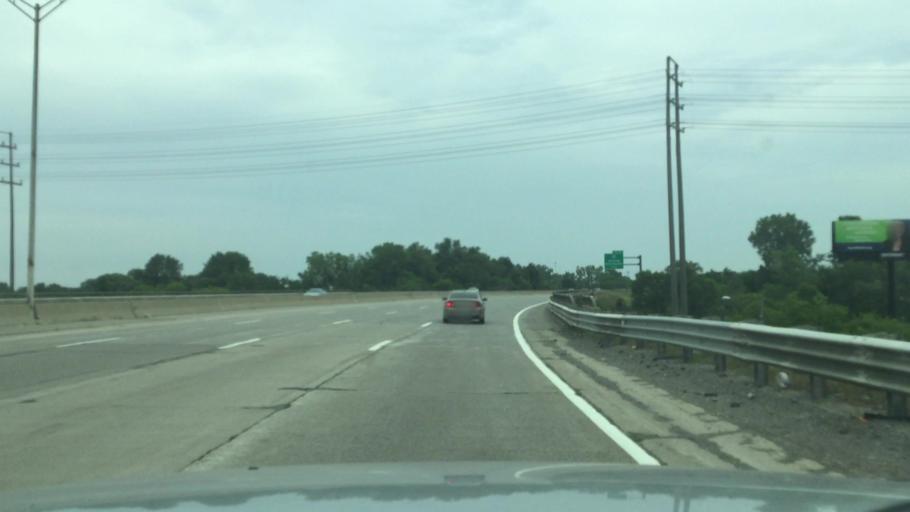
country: US
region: Michigan
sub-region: Genesee County
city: Flint
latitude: 42.9922
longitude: -83.6812
